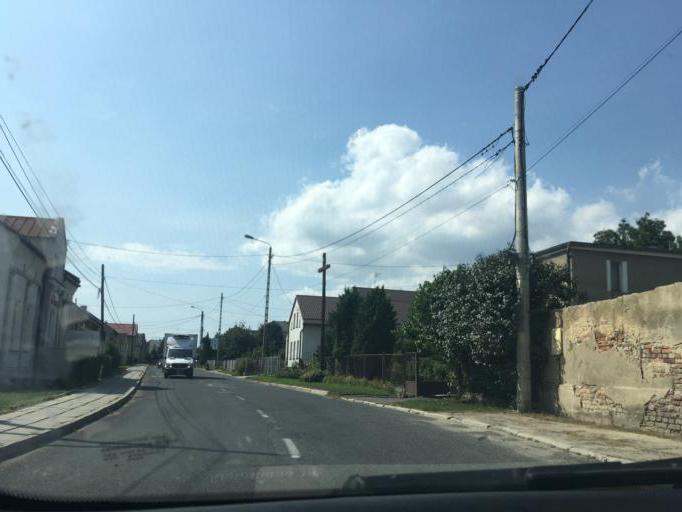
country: PL
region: Opole Voivodeship
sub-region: Powiat glubczycki
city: Kietrz
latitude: 50.0849
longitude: 18.0082
